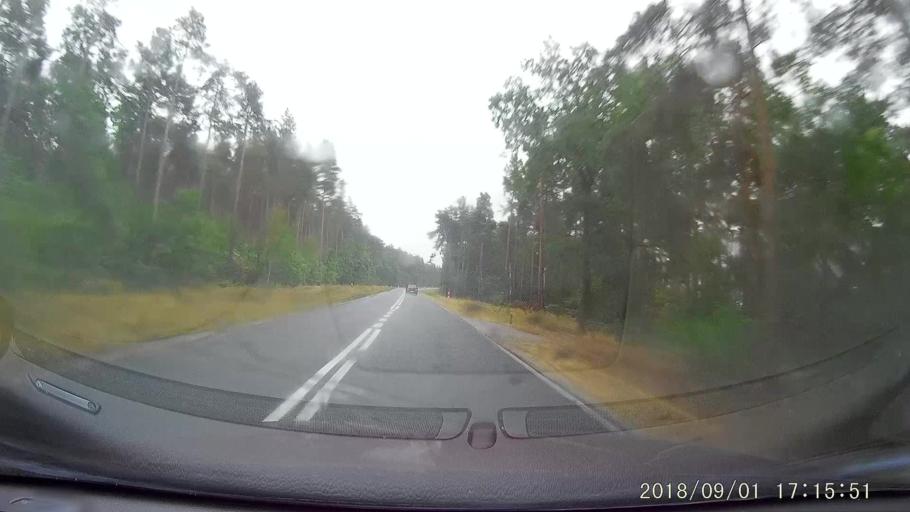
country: PL
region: Lubusz
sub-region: Powiat zielonogorski
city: Nowogrod Bobrzanski
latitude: 51.7703
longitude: 15.2659
